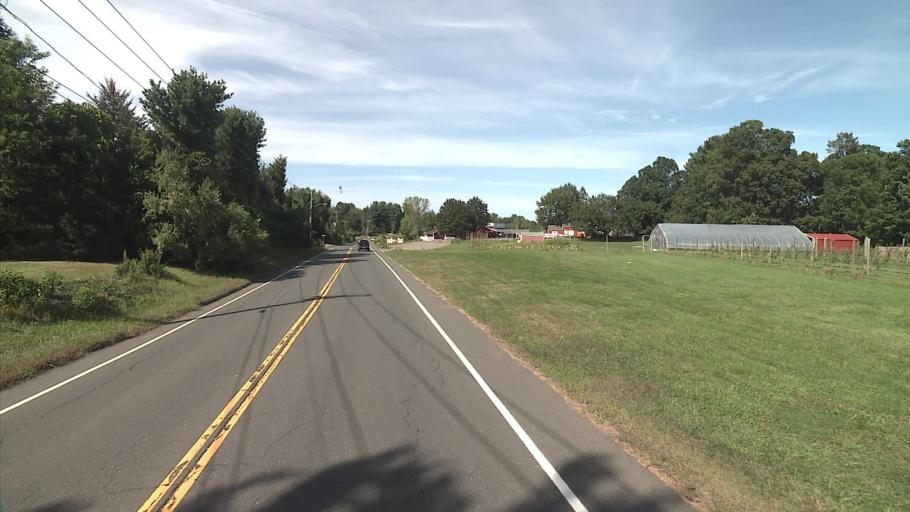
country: US
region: Connecticut
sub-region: New Haven County
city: Cheshire Village
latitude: 41.5083
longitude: -72.8751
